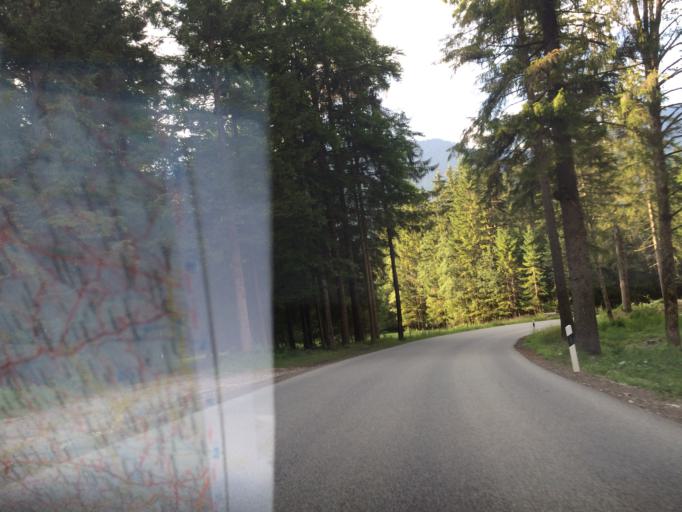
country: DE
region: Bavaria
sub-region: Upper Bavaria
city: Grainau
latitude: 47.4628
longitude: 11.0051
